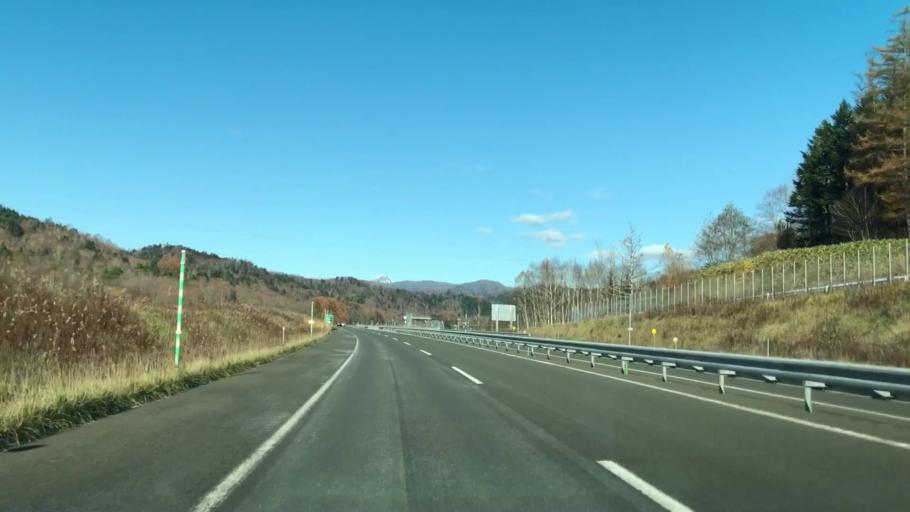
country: JP
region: Hokkaido
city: Shimo-furano
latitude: 42.9265
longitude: 142.2035
